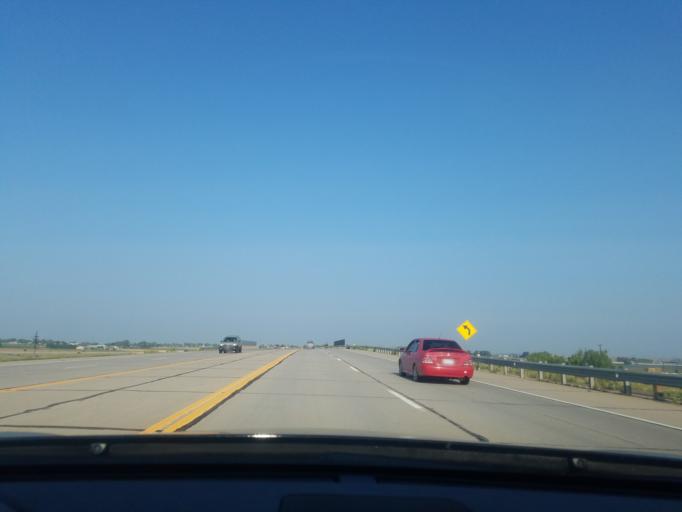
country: US
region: Colorado
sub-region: Larimer County
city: Campion
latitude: 40.3357
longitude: -105.0820
